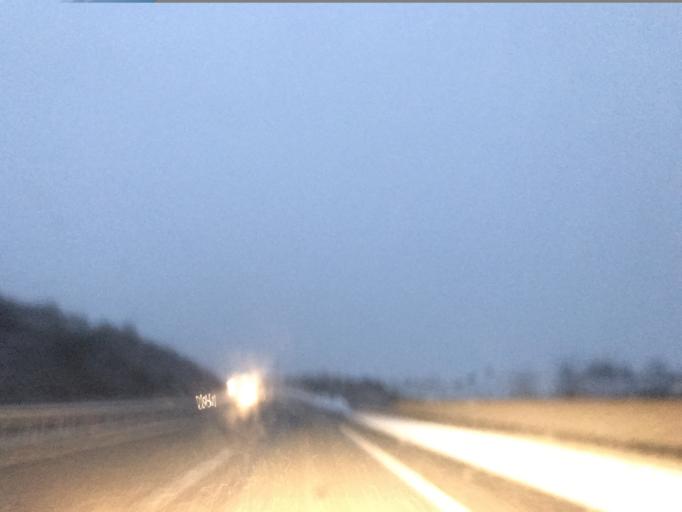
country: FR
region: Auvergne
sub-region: Departement du Puy-de-Dome
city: Charbonnieres-les-Varennes
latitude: 45.9096
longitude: 2.9536
